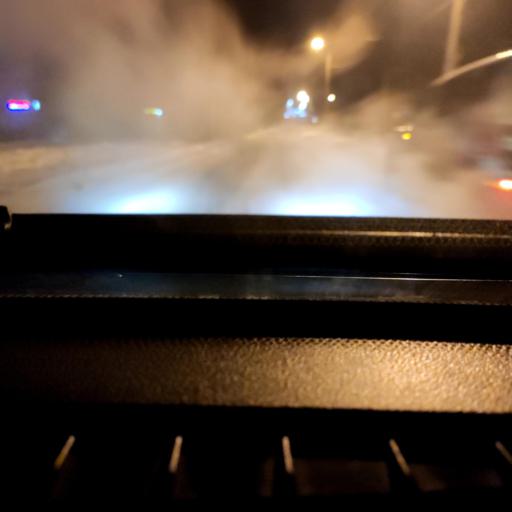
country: RU
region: Perm
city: Perm
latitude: 58.0883
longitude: 56.4077
